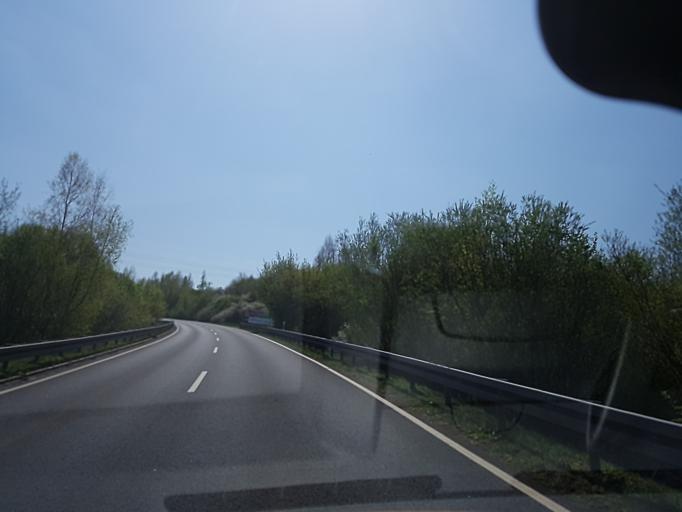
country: DE
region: Saxony
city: Leisnig
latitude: 51.1688
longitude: 12.9053
